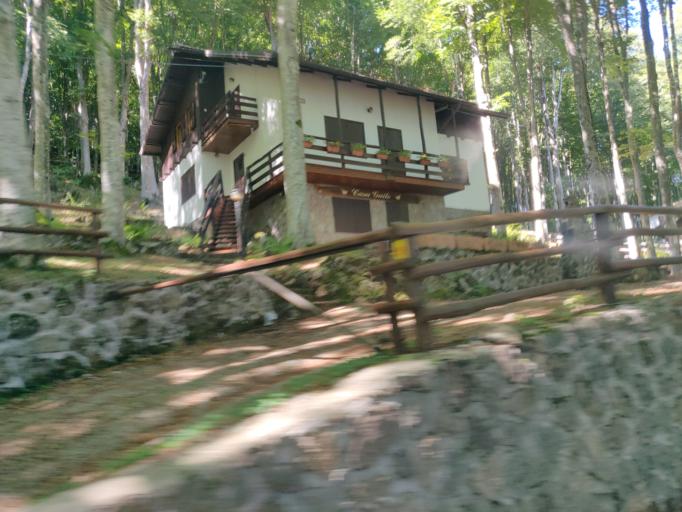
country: IT
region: Tuscany
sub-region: Provincia di Siena
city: Abbadia San Salvatore
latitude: 42.8964
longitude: 11.6283
